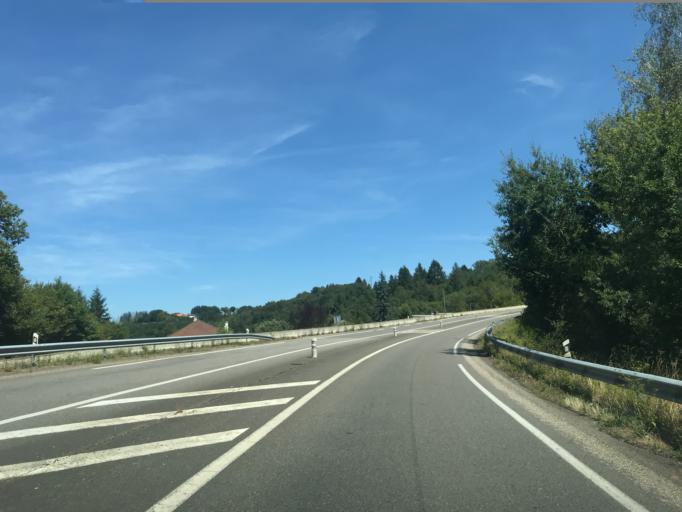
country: FR
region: Limousin
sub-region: Departement de la Correze
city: Naves
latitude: 45.2950
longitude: 1.8081
